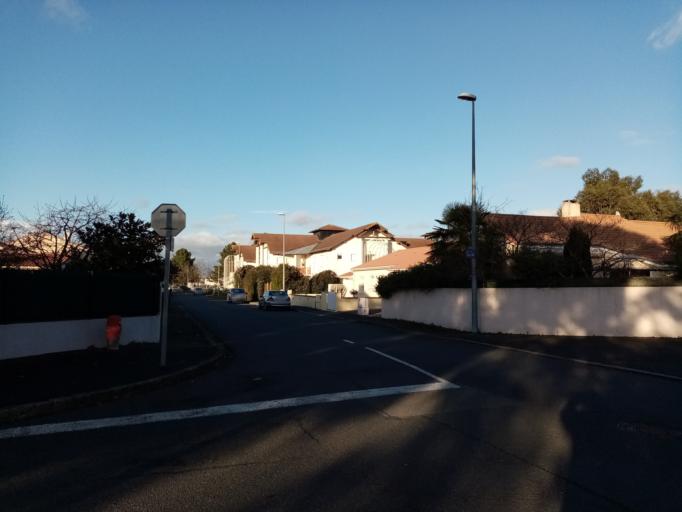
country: FR
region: Pays de la Loire
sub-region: Departement de la Loire-Atlantique
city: Saint-Sebastien-sur-Loire
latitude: 47.1907
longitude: -1.5023
